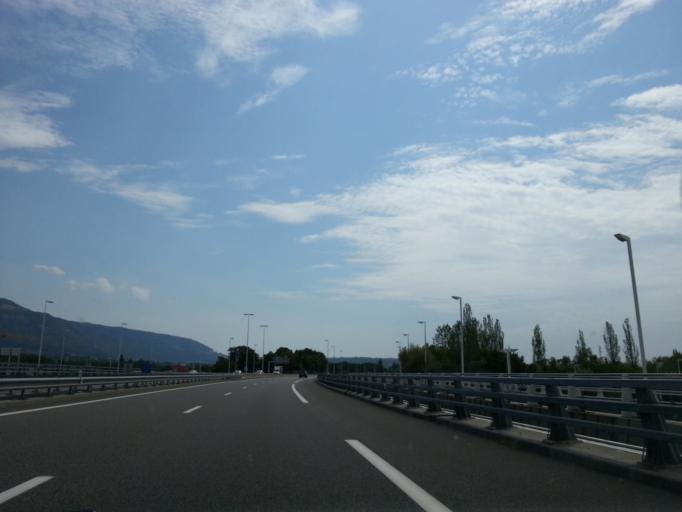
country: FR
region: Rhone-Alpes
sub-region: Departement de la Haute-Savoie
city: Neydens
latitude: 46.1339
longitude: 6.1005
